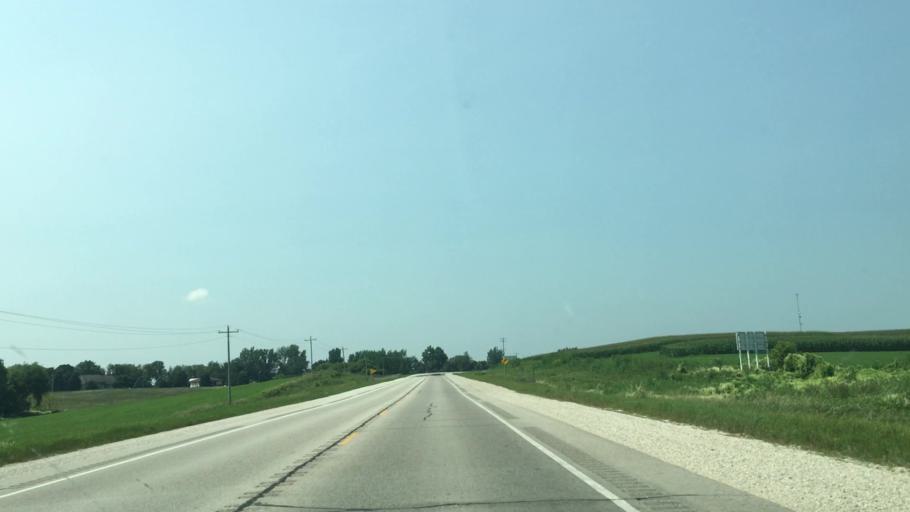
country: US
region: Iowa
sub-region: Winneshiek County
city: Decorah
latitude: 43.1919
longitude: -91.8686
